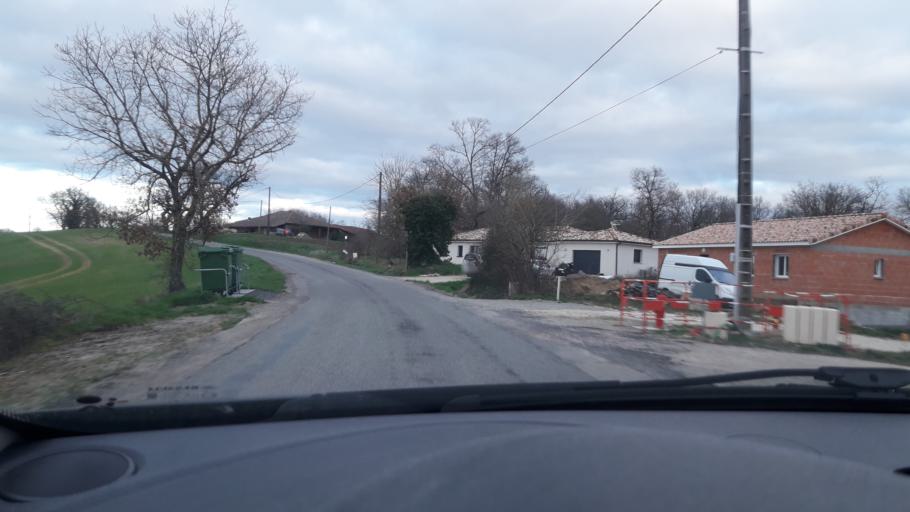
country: FR
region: Midi-Pyrenees
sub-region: Departement de la Haute-Garonne
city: Launac
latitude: 43.7167
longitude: 1.0918
